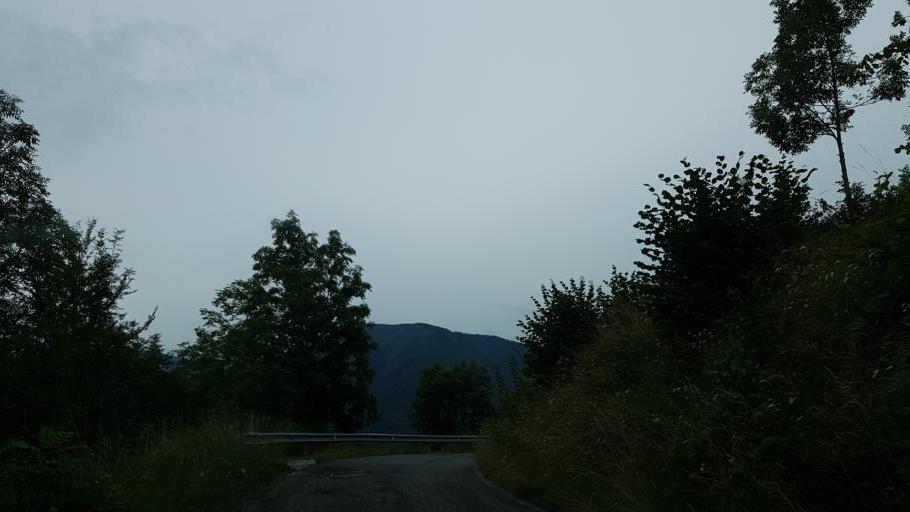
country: IT
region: Piedmont
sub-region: Provincia di Cuneo
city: Stroppo
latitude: 44.5188
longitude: 7.1203
